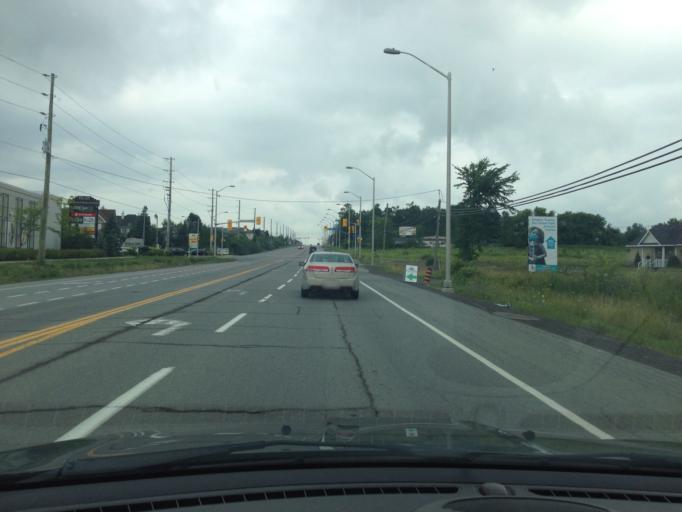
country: CA
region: Ontario
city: Ottawa
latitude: 45.3194
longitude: -75.5931
